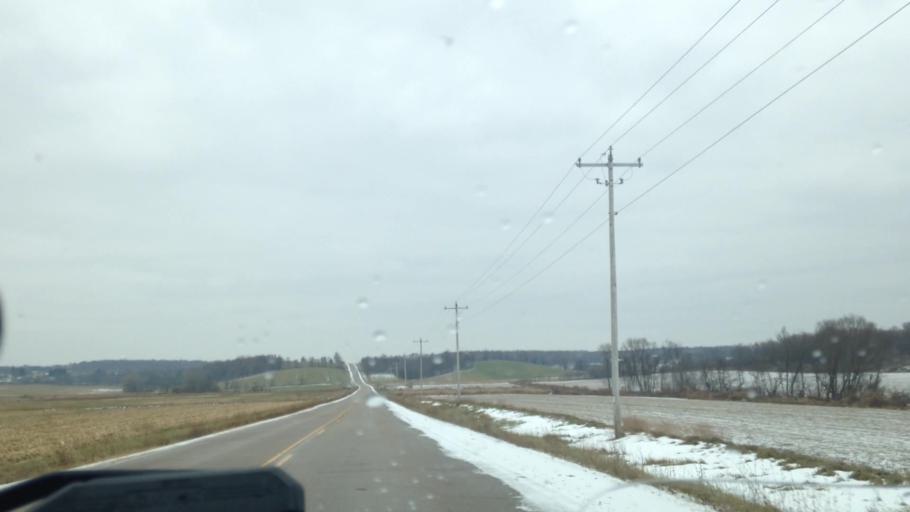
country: US
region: Wisconsin
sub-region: Dodge County
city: Mayville
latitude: 43.4708
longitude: -88.5003
